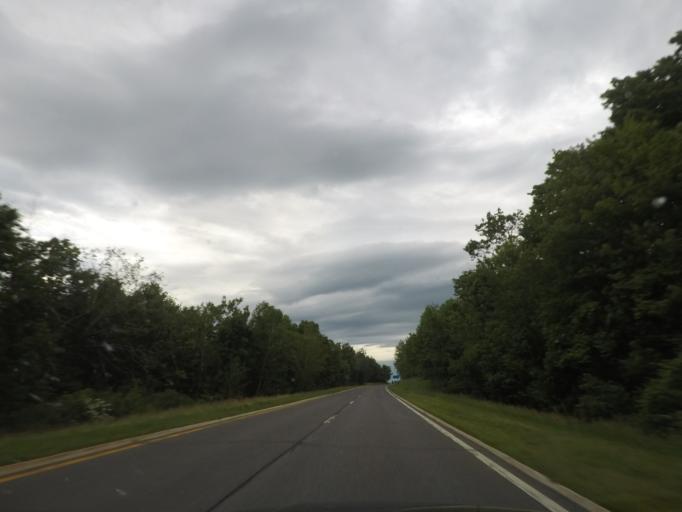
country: US
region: New York
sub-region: Dutchess County
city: Pine Plains
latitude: 42.0658
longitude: -73.7265
